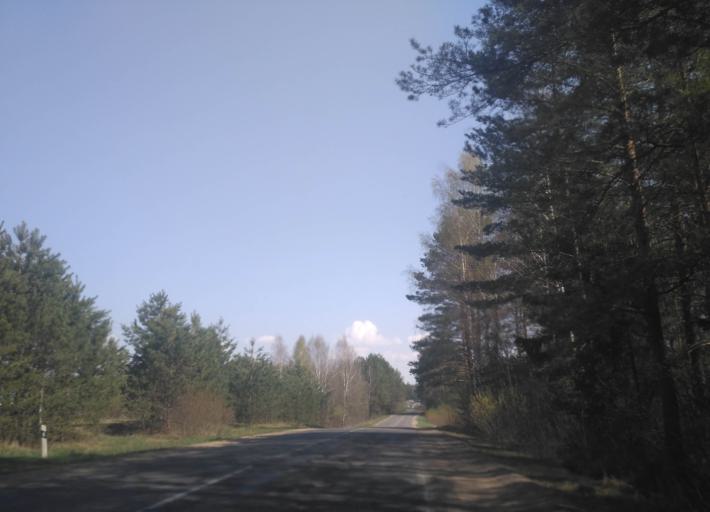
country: BY
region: Minsk
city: Loshnitsa
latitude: 54.4183
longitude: 28.6397
